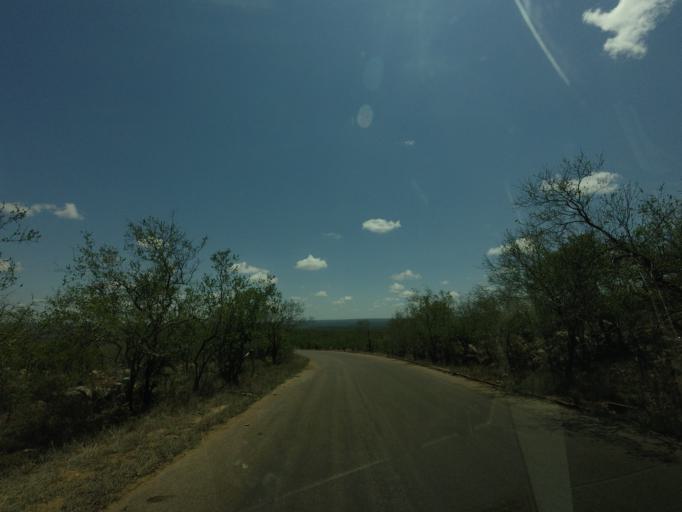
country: ZA
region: Mpumalanga
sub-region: Ehlanzeni District
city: Komatipoort
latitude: -24.8456
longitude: 31.8942
